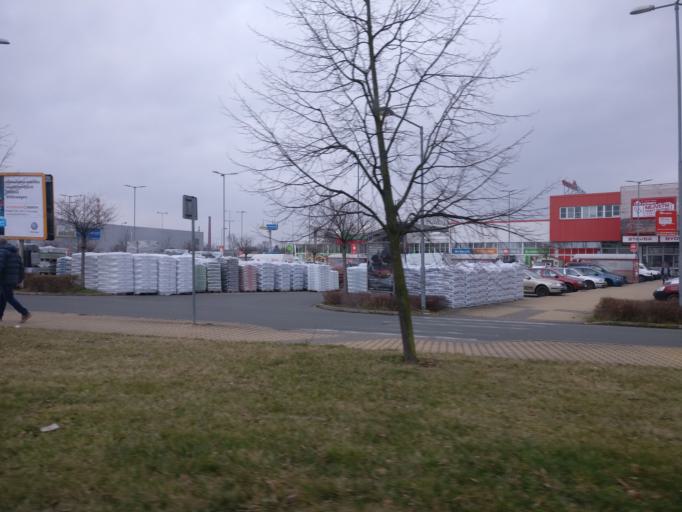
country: CZ
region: Pardubicky
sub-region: Okres Pardubice
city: Pardubice
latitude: 50.0361
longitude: 15.7540
